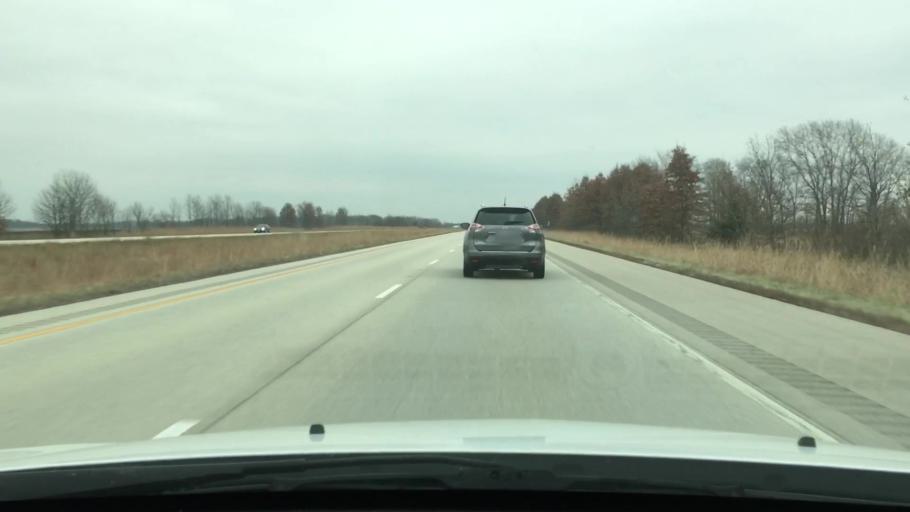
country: US
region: Illinois
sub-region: Sangamon County
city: New Berlin
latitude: 39.7450
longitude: -89.8156
